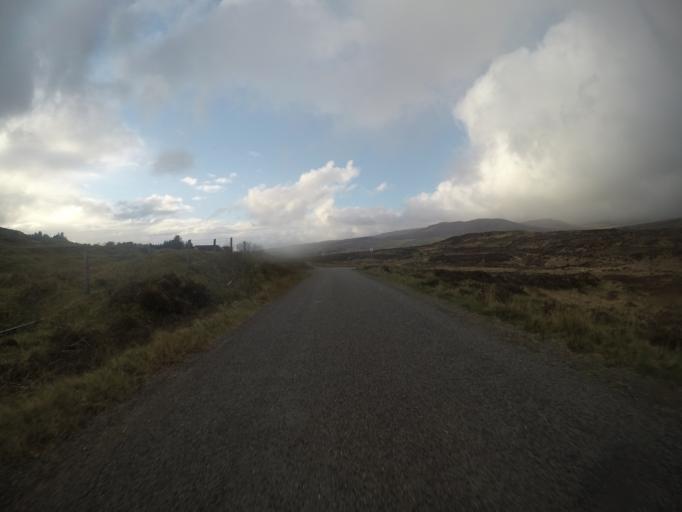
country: GB
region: Scotland
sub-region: Highland
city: Isle of Skye
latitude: 57.4648
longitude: -6.2974
